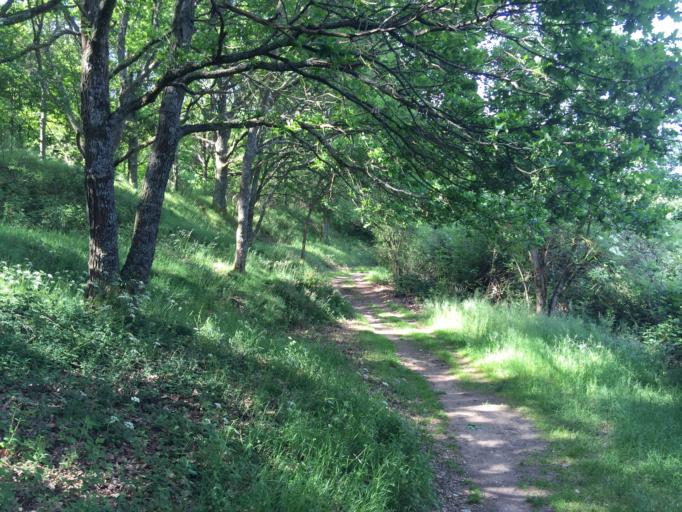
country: FR
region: Rhone-Alpes
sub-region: Departement de la Loire
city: Saint-Priest-en-Jarez
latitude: 45.4537
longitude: 4.3714
